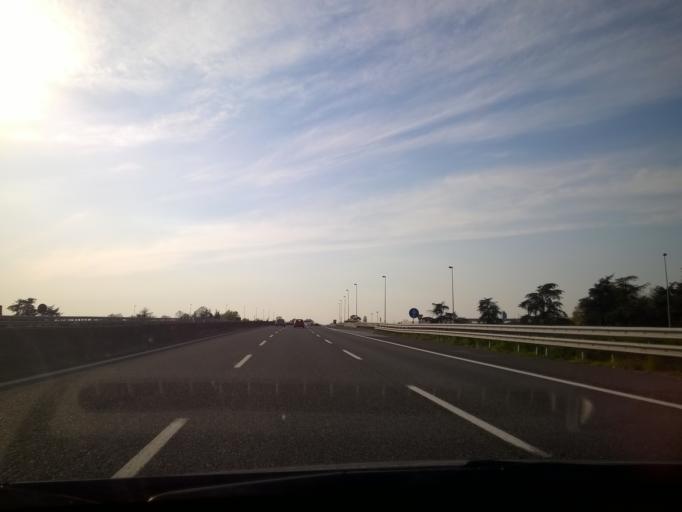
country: IT
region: Emilia-Romagna
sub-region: Forli-Cesena
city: Forli
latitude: 44.2518
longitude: 12.0921
